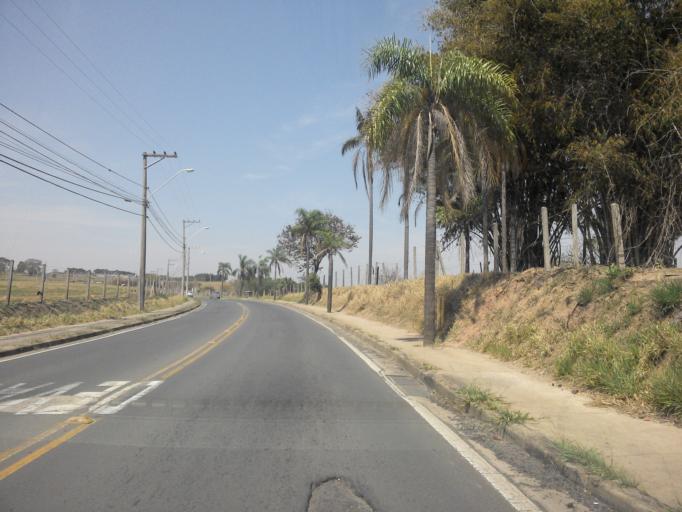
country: BR
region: Sao Paulo
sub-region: Hortolandia
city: Hortolandia
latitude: -22.9278
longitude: -47.1891
